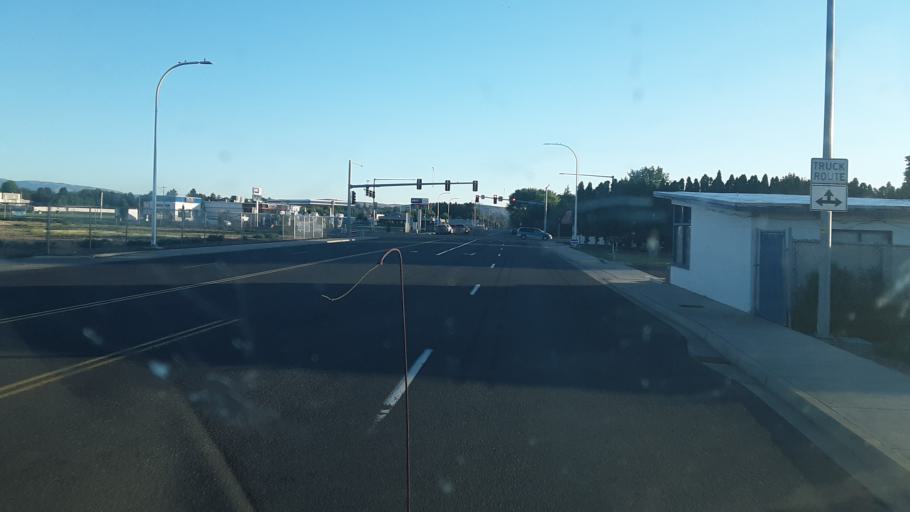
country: US
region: Washington
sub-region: Yakima County
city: Yakima
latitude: 46.5694
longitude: -120.5304
